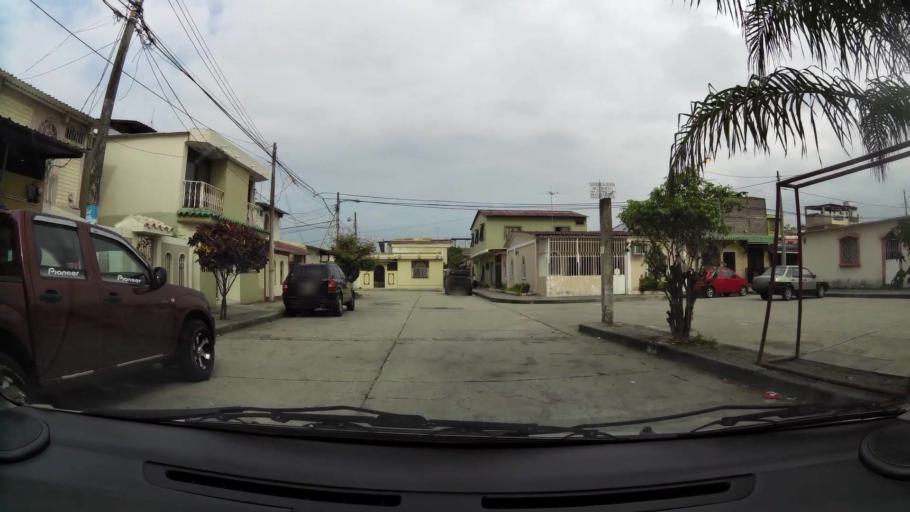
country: EC
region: Guayas
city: Eloy Alfaro
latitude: -2.1385
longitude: -79.8857
